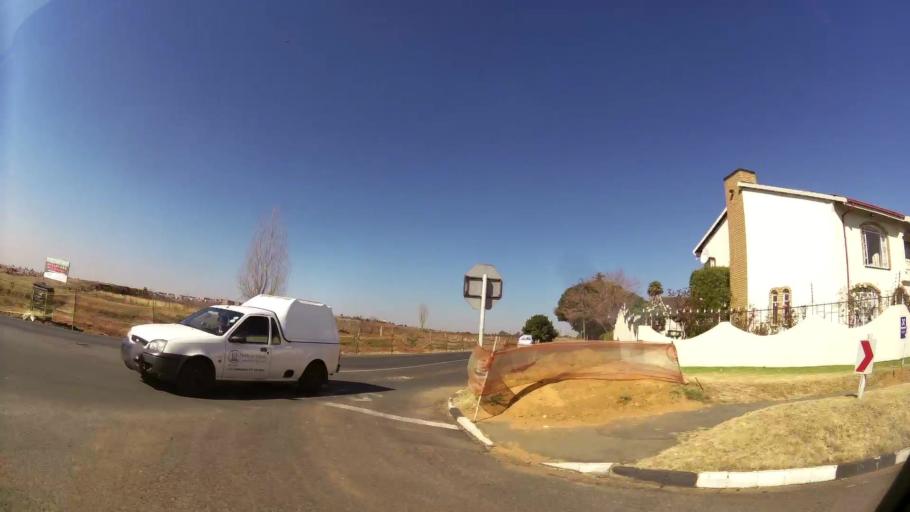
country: ZA
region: Gauteng
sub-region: City of Johannesburg Metropolitan Municipality
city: Johannesburg
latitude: -26.2471
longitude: 28.0714
